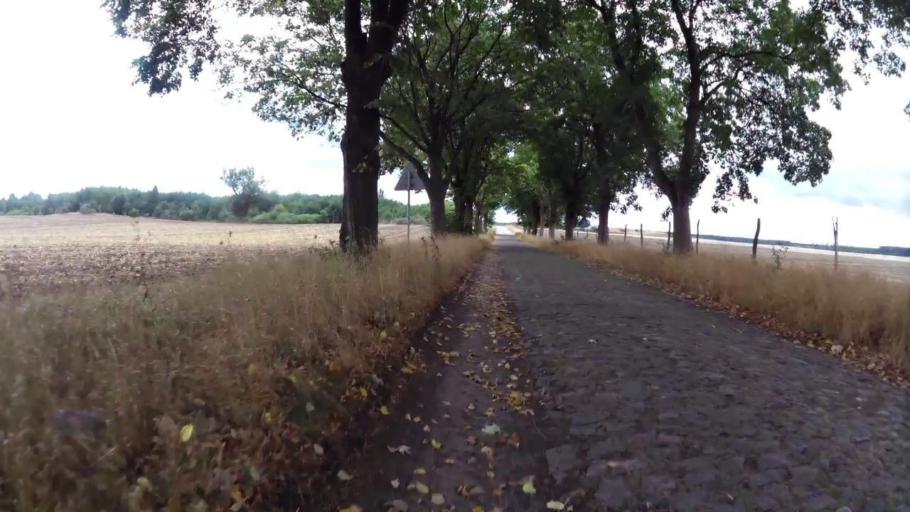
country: PL
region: West Pomeranian Voivodeship
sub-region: Powiat mysliborski
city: Debno
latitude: 52.8384
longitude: 14.7142
